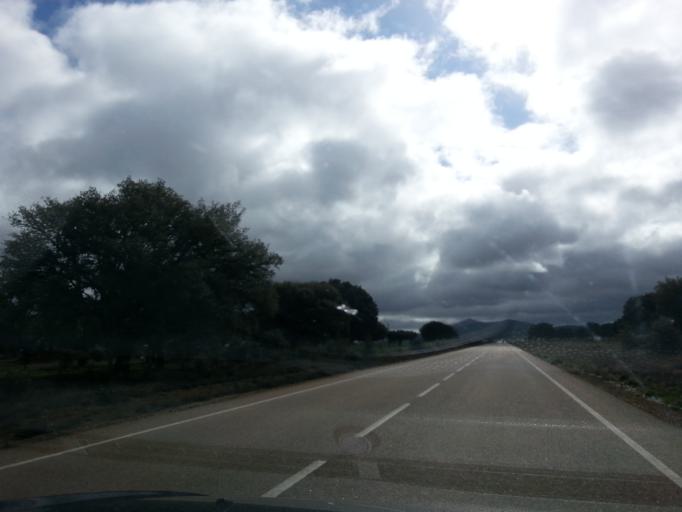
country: ES
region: Castille and Leon
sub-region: Provincia de Salamanca
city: Abusejo
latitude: 40.6817
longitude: -6.1302
